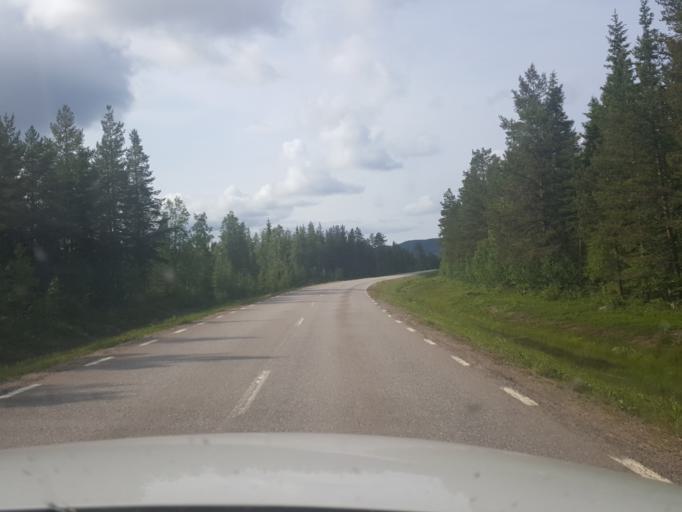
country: SE
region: Norrbotten
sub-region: Arjeplogs Kommun
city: Arjeplog
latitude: 65.6162
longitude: 18.0826
